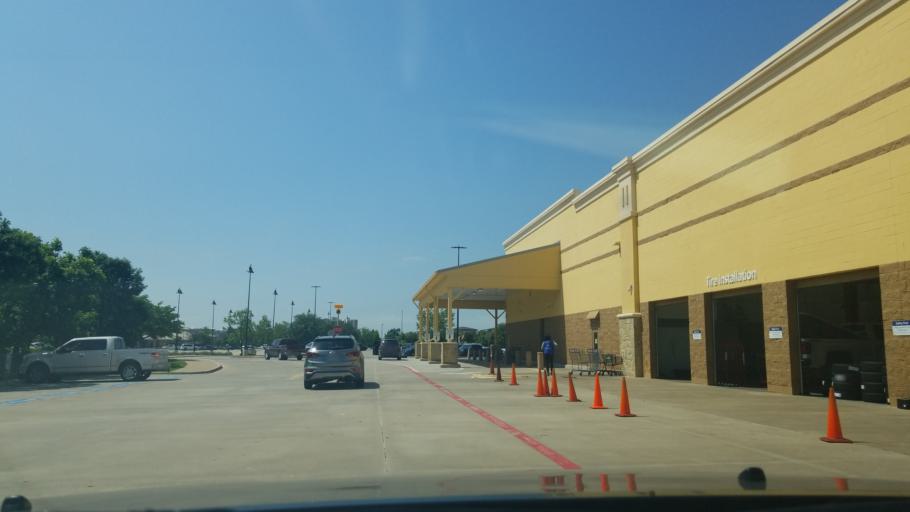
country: US
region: Texas
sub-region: Denton County
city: Denton
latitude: 33.2330
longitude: -97.1693
